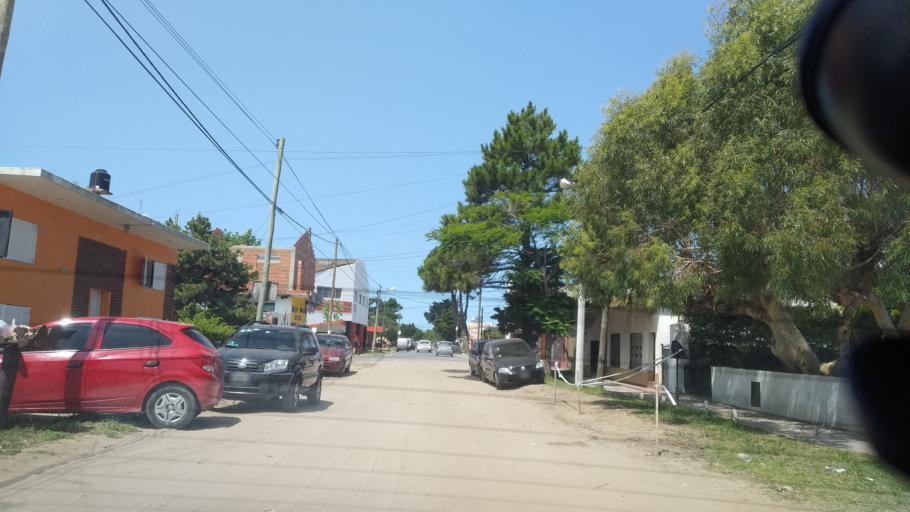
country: AR
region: Buenos Aires
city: Mar del Tuyu
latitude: -36.5834
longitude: -56.6906
